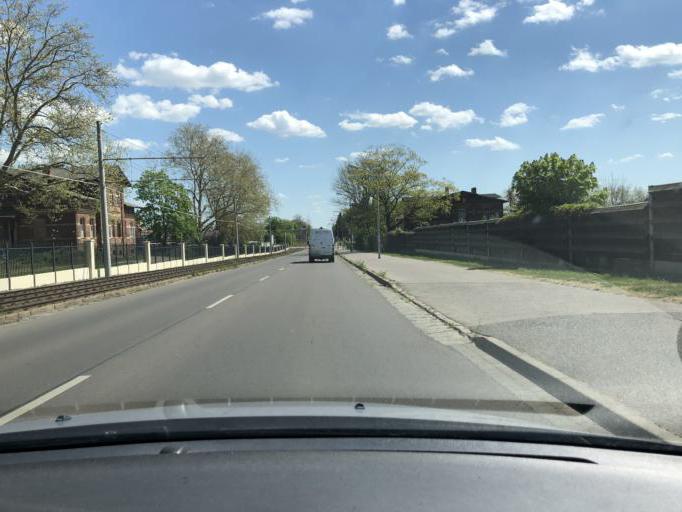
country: DE
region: Saxony
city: Schkeuditz
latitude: 51.3923
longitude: 12.2341
